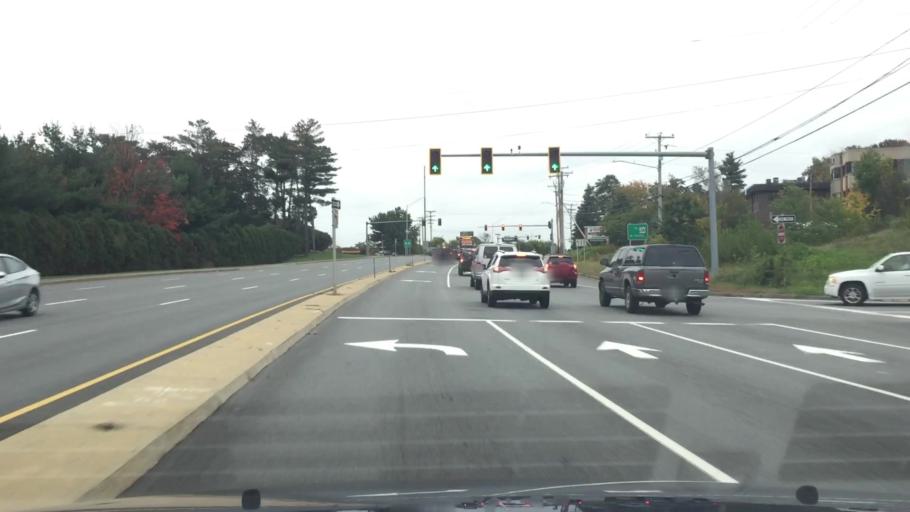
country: US
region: New Hampshire
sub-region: Hillsborough County
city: Hudson
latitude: 42.7222
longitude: -71.4437
